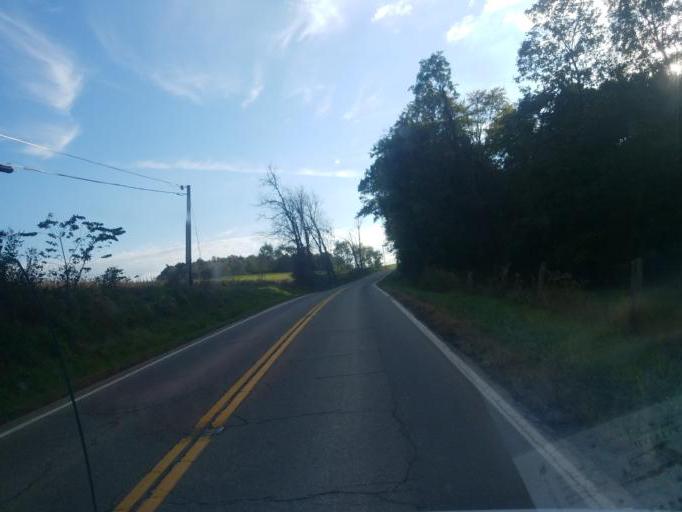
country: US
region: Ohio
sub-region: Wayne County
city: Shreve
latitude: 40.6228
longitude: -82.0901
